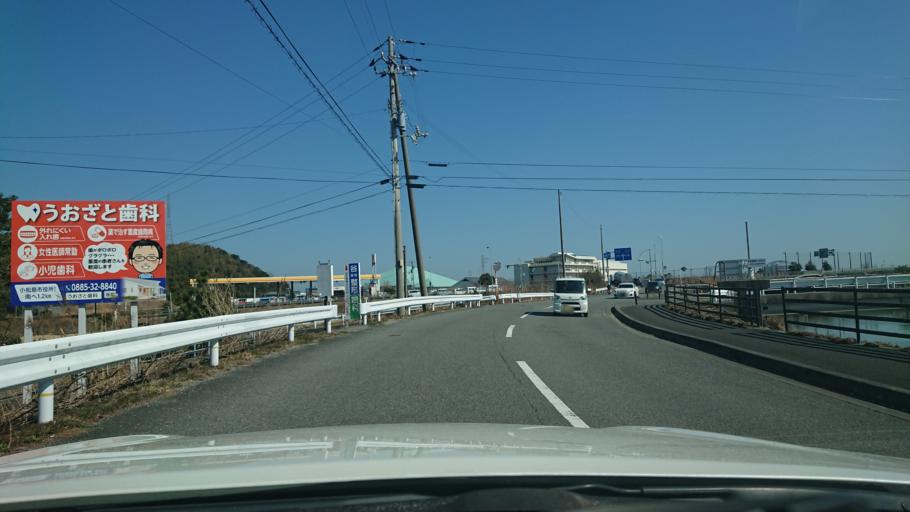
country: JP
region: Tokushima
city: Komatsushimacho
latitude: 33.9765
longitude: 134.6035
